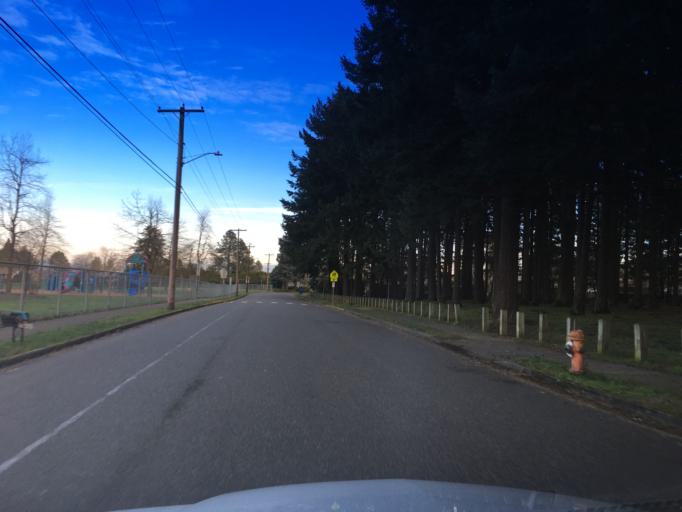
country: US
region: Oregon
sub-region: Multnomah County
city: Lents
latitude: 45.5409
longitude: -122.5313
